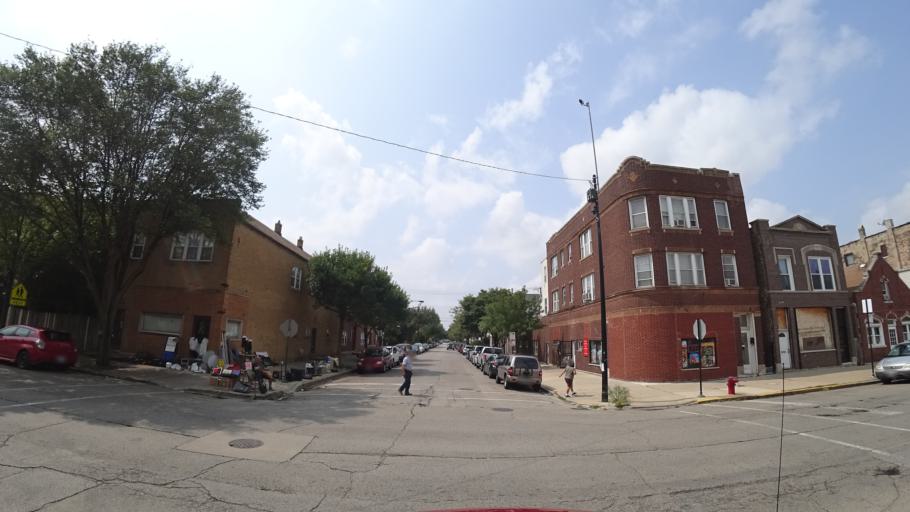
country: US
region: Illinois
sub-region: Cook County
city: Chicago
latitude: 41.8494
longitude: -87.6806
